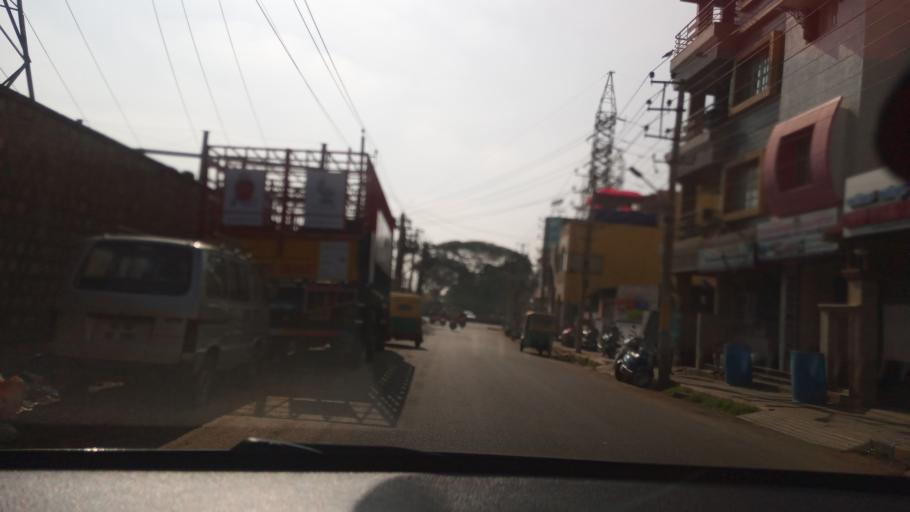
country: IN
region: Karnataka
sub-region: Bangalore Urban
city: Yelahanka
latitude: 13.0445
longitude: 77.5532
